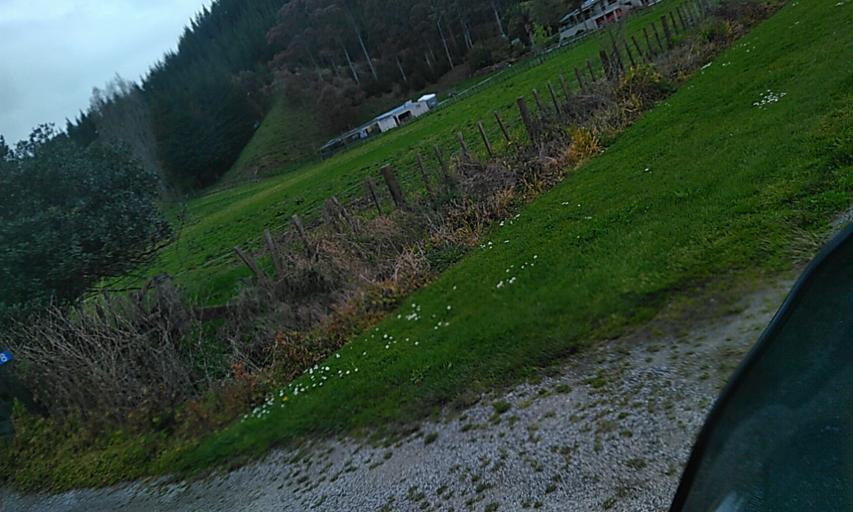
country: NZ
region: Gisborne
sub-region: Gisborne District
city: Gisborne
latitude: -38.5541
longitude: 177.9239
